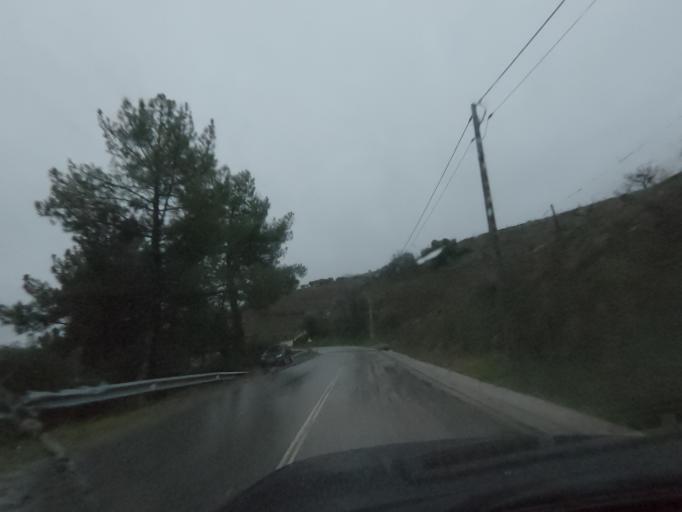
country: PT
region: Vila Real
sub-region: Sabrosa
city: Sabrosa
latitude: 41.2249
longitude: -7.5551
